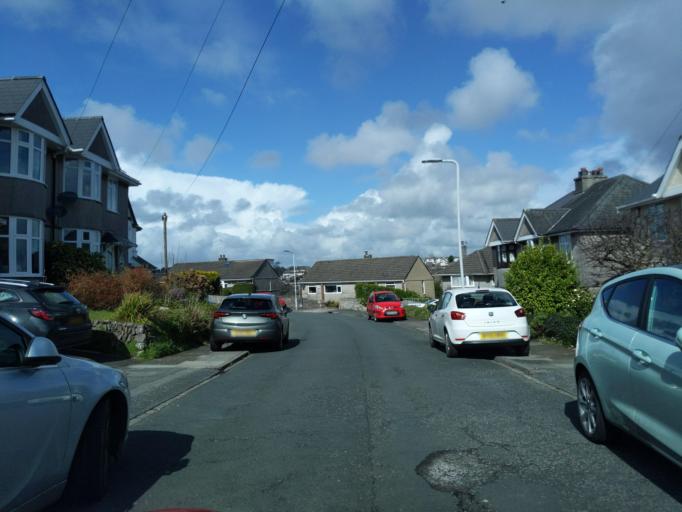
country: GB
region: England
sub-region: Plymouth
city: Plymouth
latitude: 50.3936
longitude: -4.1216
